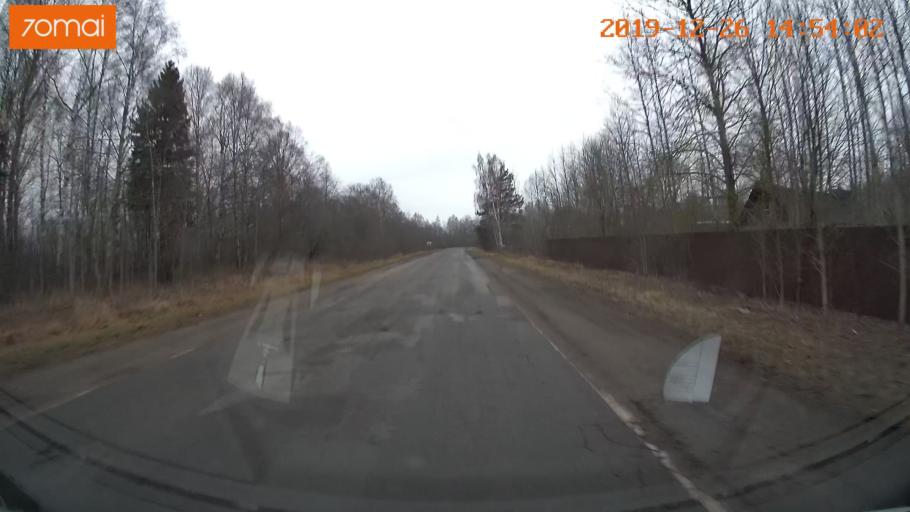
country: RU
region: Jaroslavl
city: Rybinsk
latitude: 58.3104
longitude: 38.8863
